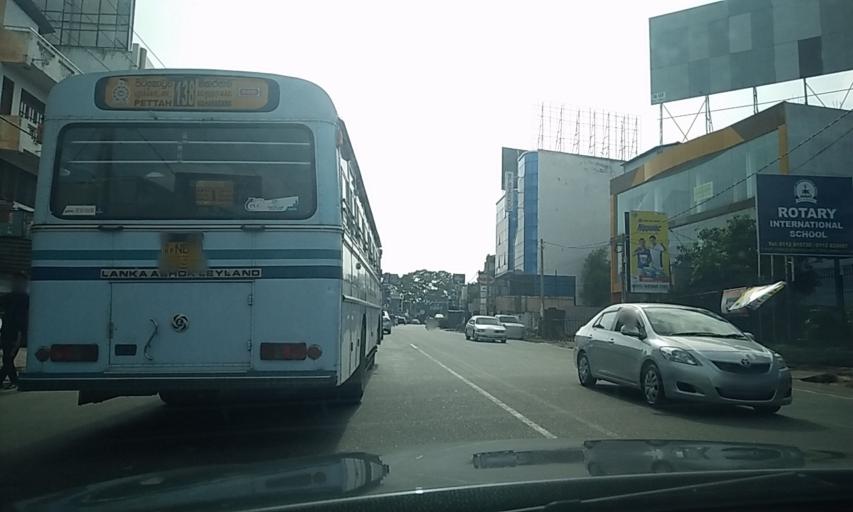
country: LK
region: Western
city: Sri Jayewardenepura Kotte
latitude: 6.8632
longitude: 79.9005
